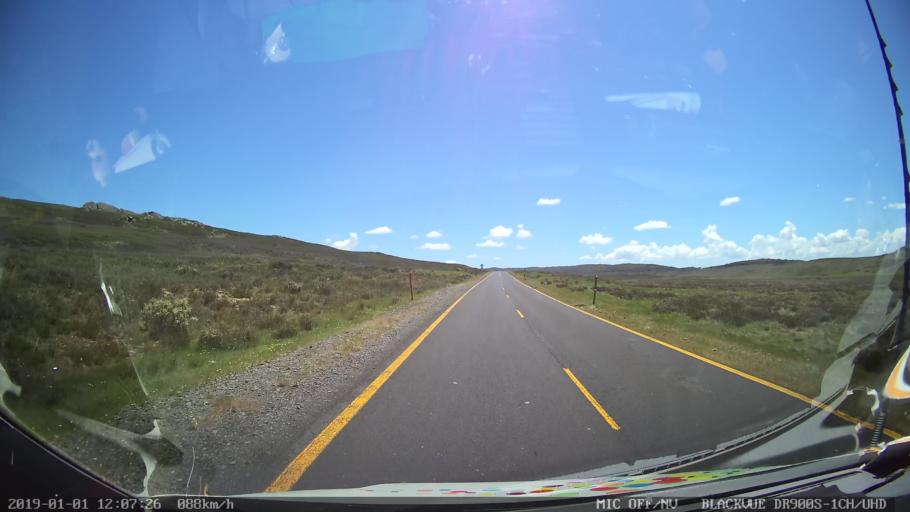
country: AU
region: New South Wales
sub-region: Tumut Shire
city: Tumut
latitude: -35.8331
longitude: 148.4898
